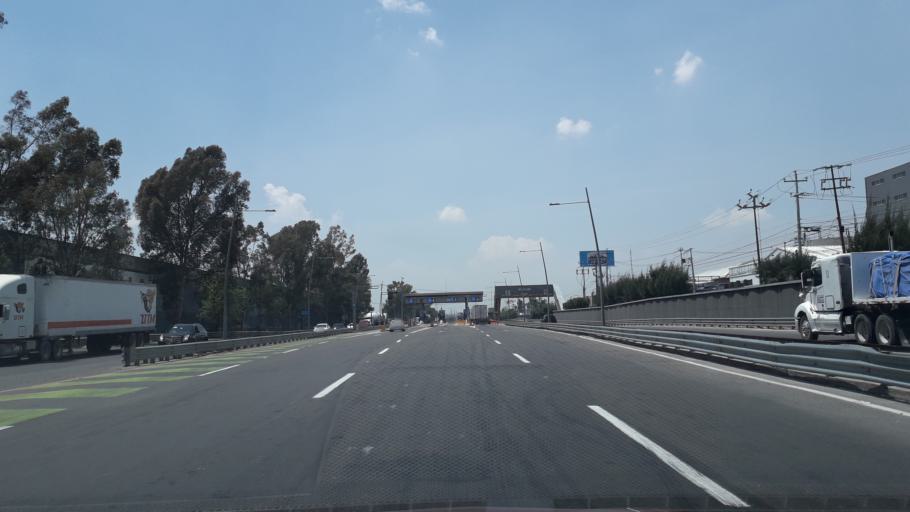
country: MX
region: Puebla
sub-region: Puebla
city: San Sebastian de Aparicio
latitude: 19.0764
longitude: -98.1482
